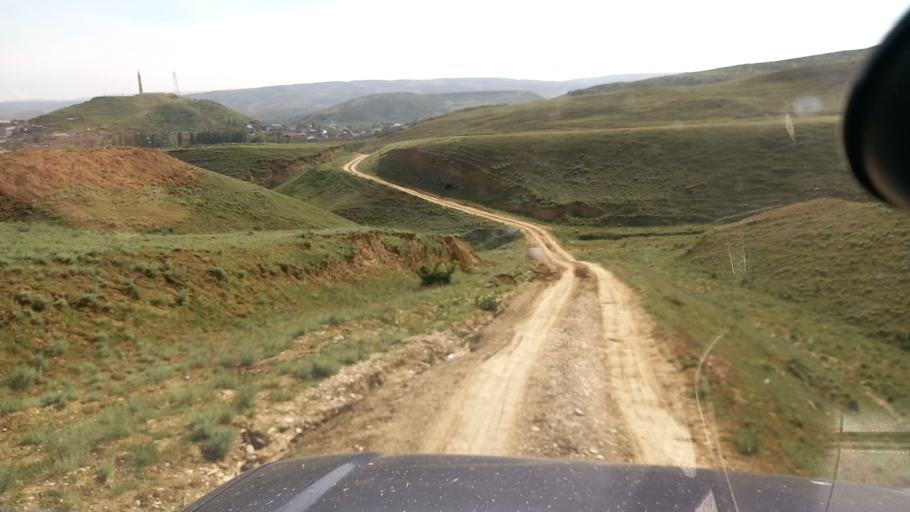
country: RU
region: Dagestan
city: Karabudakhkent
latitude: 42.7193
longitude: 47.5691
